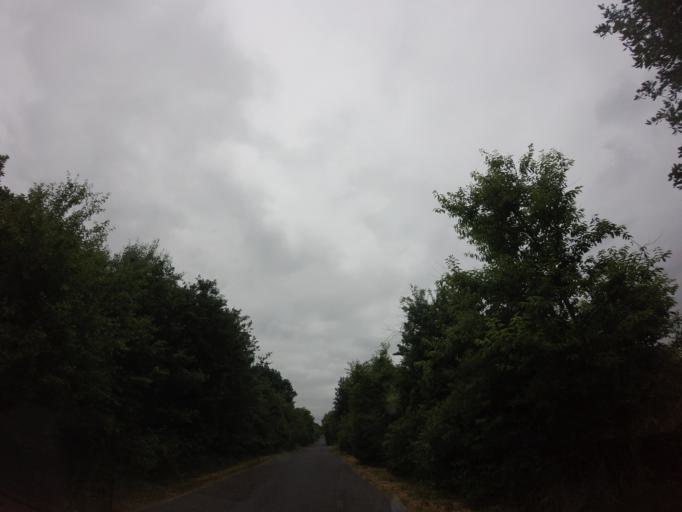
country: PL
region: West Pomeranian Voivodeship
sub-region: Powiat choszczenski
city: Bierzwnik
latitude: 53.1479
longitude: 15.6490
